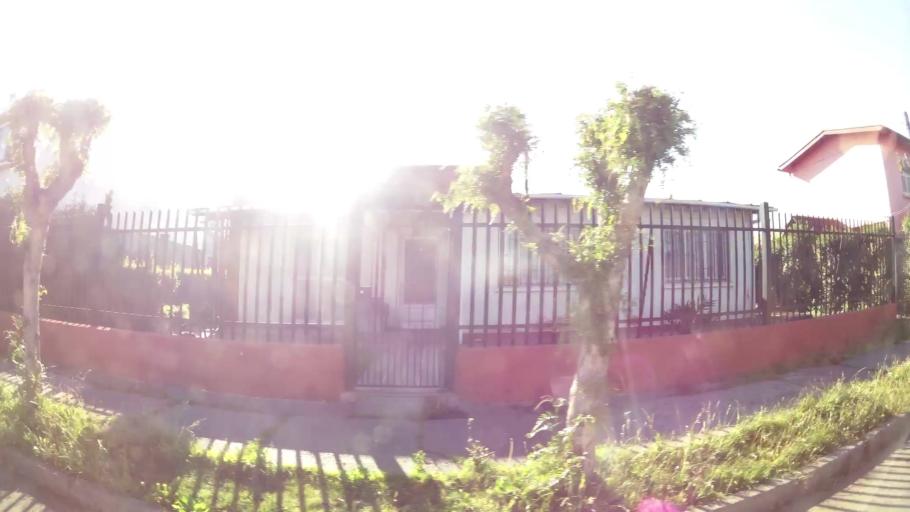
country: CL
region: Santiago Metropolitan
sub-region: Provincia de Maipo
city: San Bernardo
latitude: -33.5464
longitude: -70.6744
